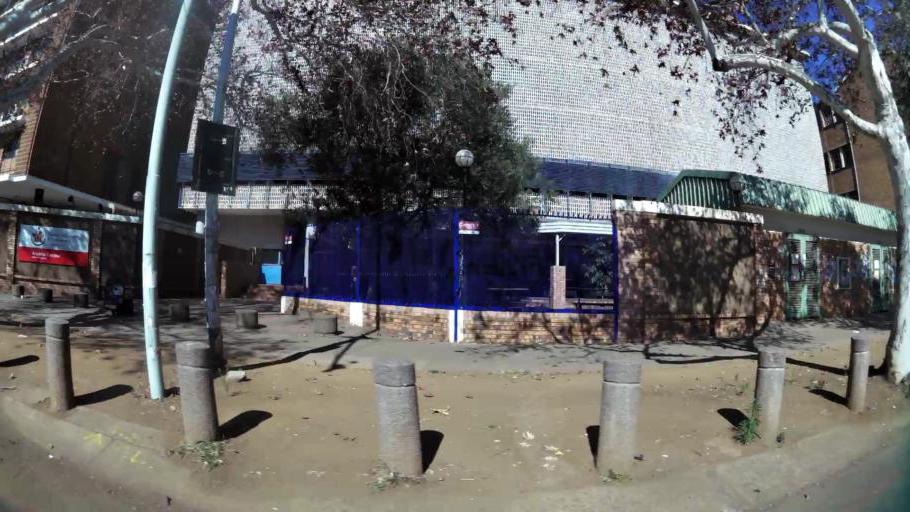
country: ZA
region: Gauteng
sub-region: City of Tshwane Metropolitan Municipality
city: Pretoria
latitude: -25.7443
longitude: 28.1994
